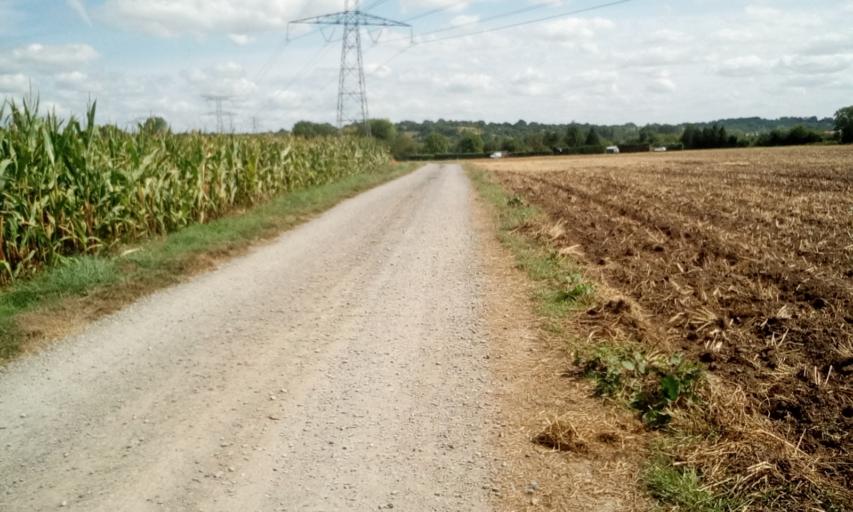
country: FR
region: Lower Normandy
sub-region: Departement du Calvados
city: Argences
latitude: 49.1346
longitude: -0.1815
